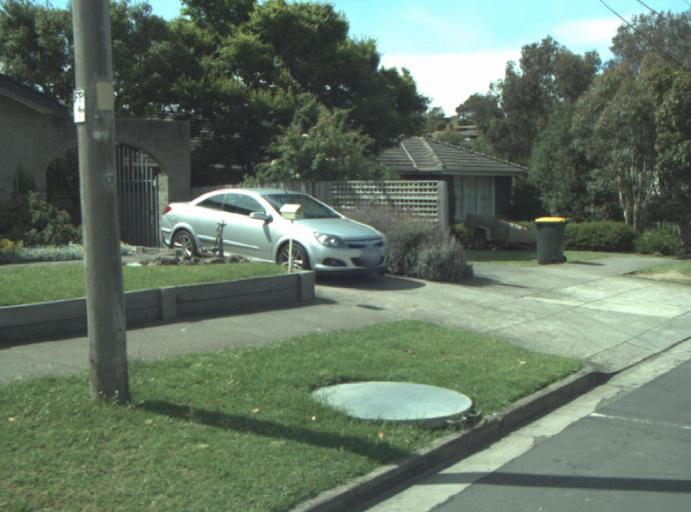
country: AU
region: Victoria
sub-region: Greater Geelong
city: Wandana Heights
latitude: -38.1704
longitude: 144.3095
